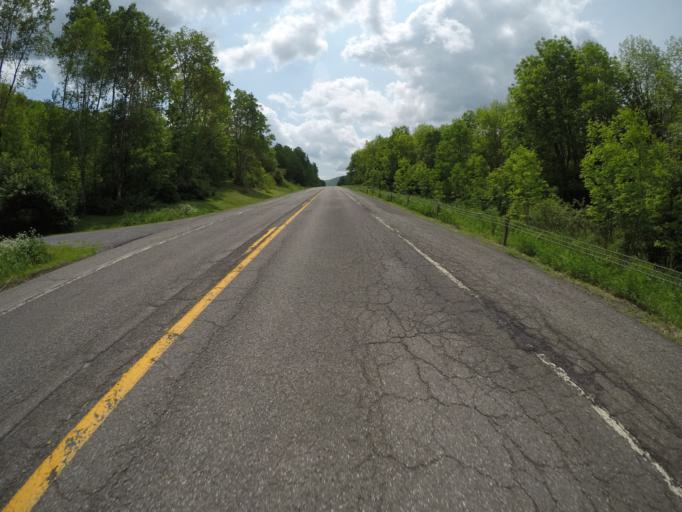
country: US
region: New York
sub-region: Delaware County
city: Stamford
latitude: 42.2651
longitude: -74.5838
